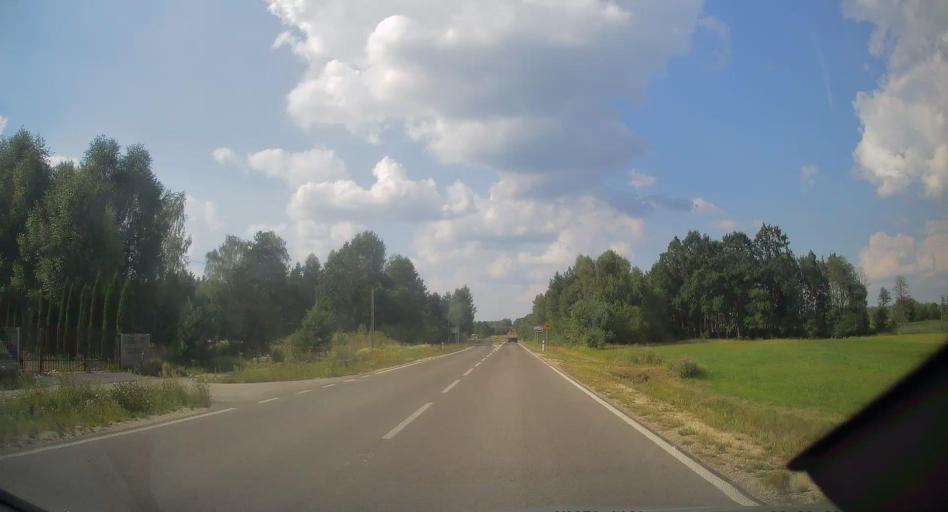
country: PL
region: Swietokrzyskie
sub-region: Powiat konecki
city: Radoszyce
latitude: 51.0574
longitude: 20.2786
